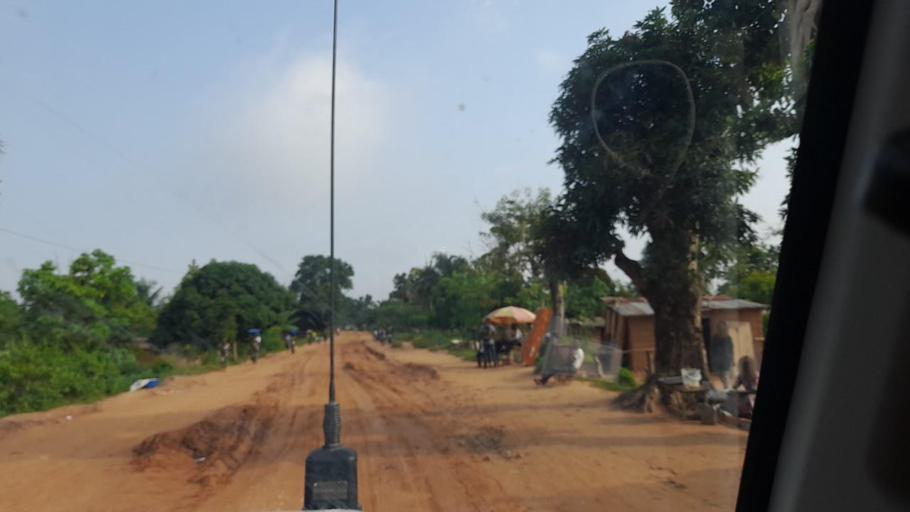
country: CD
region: Kasai-Occidental
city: Kananga
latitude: -5.8937
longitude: 22.3759
